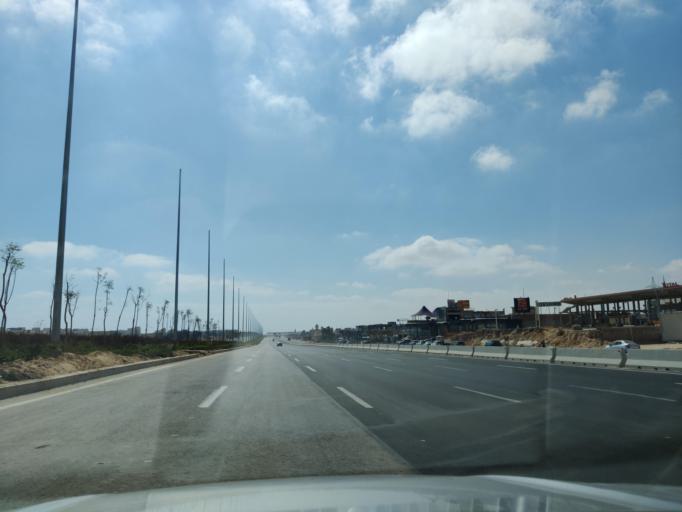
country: EG
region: Muhafazat Matruh
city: Al `Alamayn
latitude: 30.9914
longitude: 28.6779
